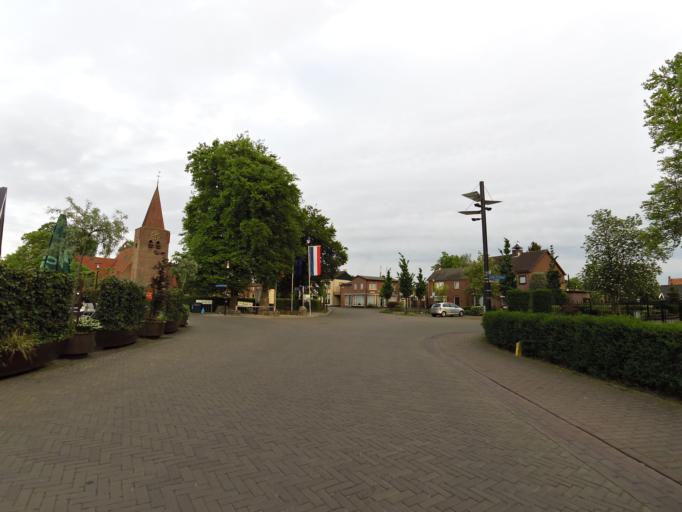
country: NL
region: Gelderland
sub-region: Oude IJsselstreek
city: Gendringen
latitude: 51.8381
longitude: 6.3922
